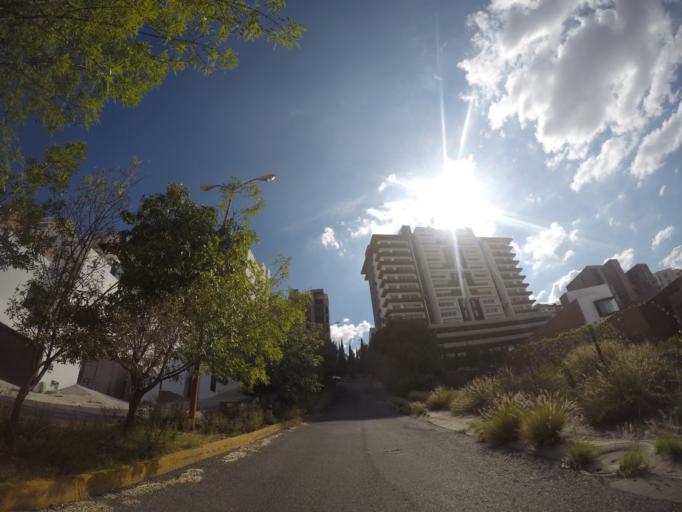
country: MX
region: San Luis Potosi
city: Escalerillas
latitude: 22.1229
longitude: -101.0329
